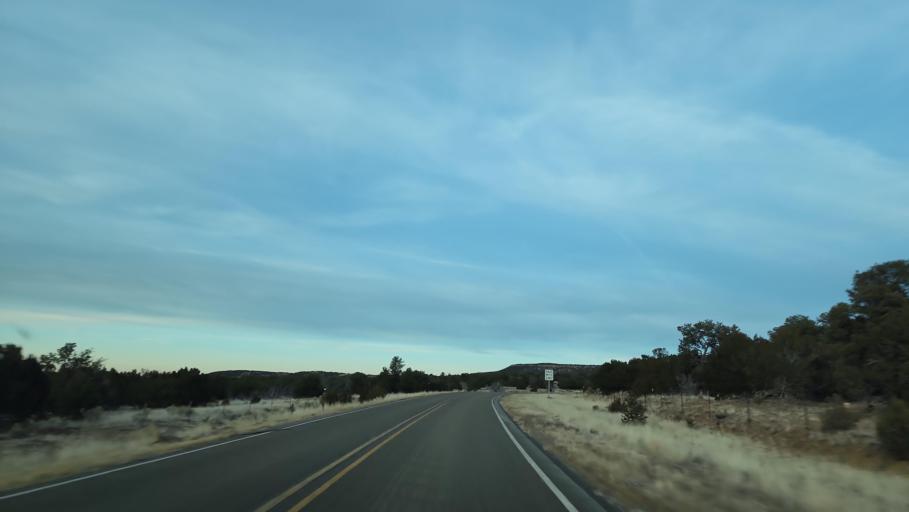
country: US
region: New Mexico
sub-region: Cibola County
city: Grants
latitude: 34.7277
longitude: -107.9734
